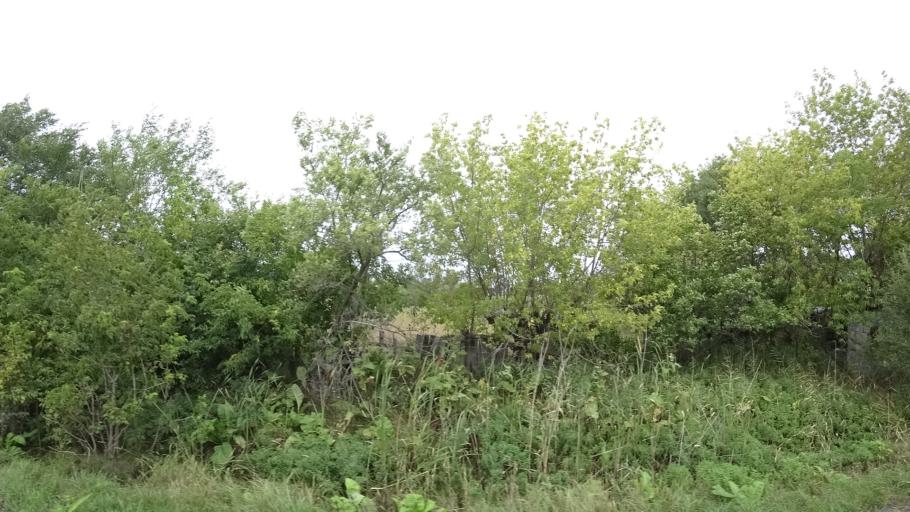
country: RU
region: Primorskiy
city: Chernigovka
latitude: 44.3340
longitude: 132.5655
